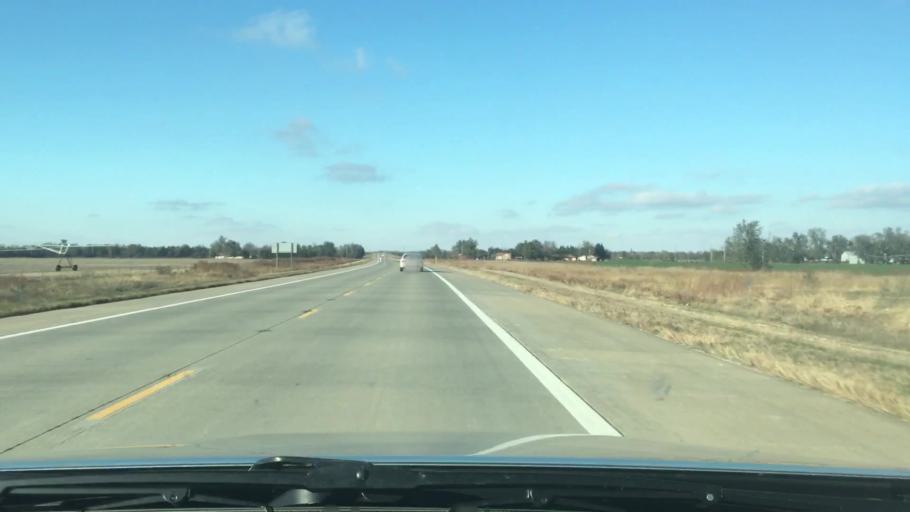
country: US
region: Kansas
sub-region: Reno County
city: Hutchinson
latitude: 38.0662
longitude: -97.9862
